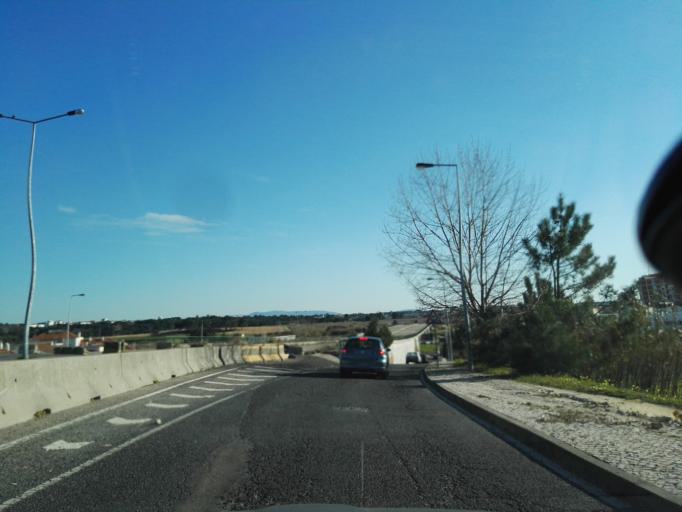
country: PT
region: Setubal
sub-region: Seixal
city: Corroios
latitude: 38.6440
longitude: -9.1499
